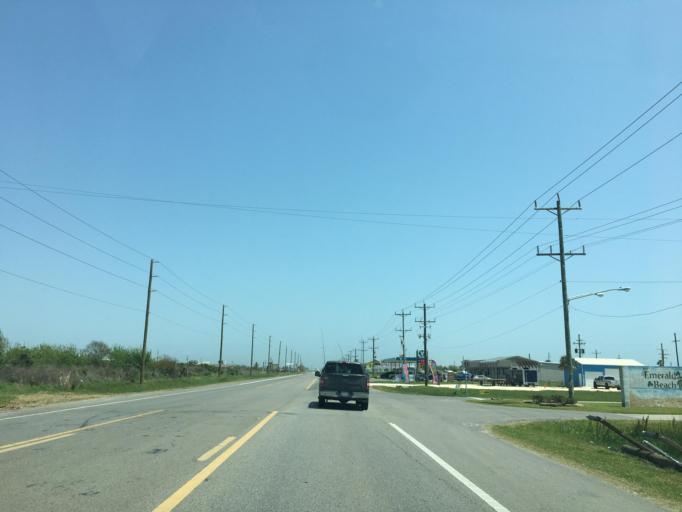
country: US
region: Texas
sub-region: Galveston County
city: Bolivar Peninsula
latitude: 29.4477
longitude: -94.6568
